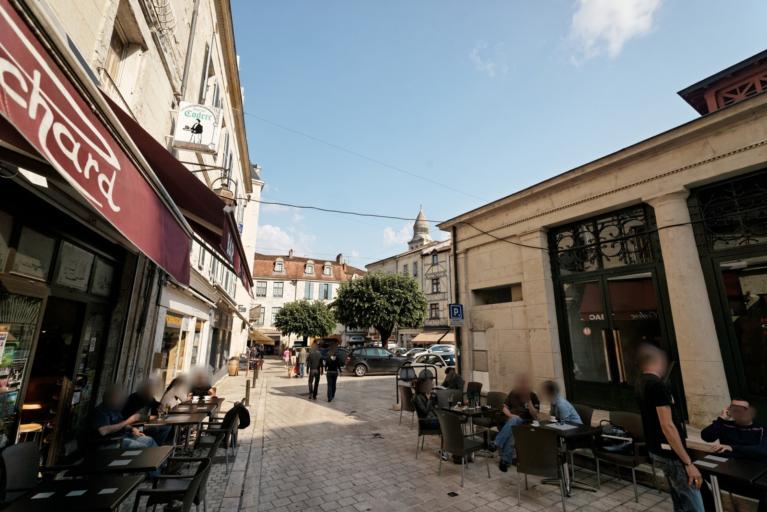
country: FR
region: Aquitaine
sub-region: Departement de la Dordogne
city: Perigueux
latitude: 45.1844
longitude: 0.7211
